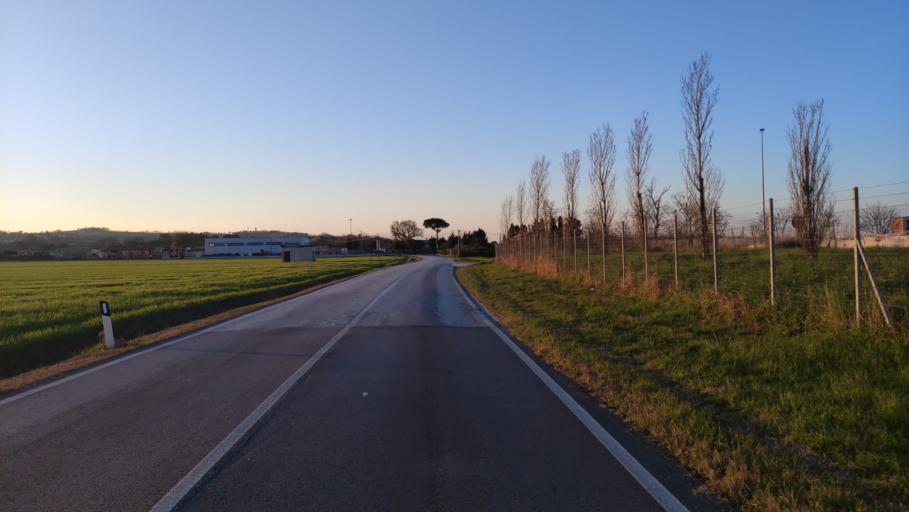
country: IT
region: The Marches
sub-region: Provincia di Pesaro e Urbino
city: Marotta
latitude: 43.7529
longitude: 13.1446
